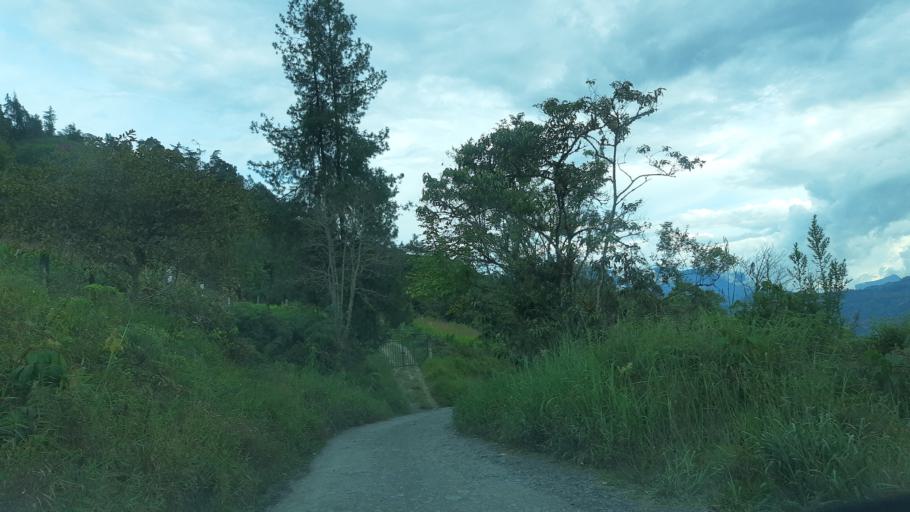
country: CO
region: Boyaca
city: Garagoa
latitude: 4.9842
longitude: -73.3230
